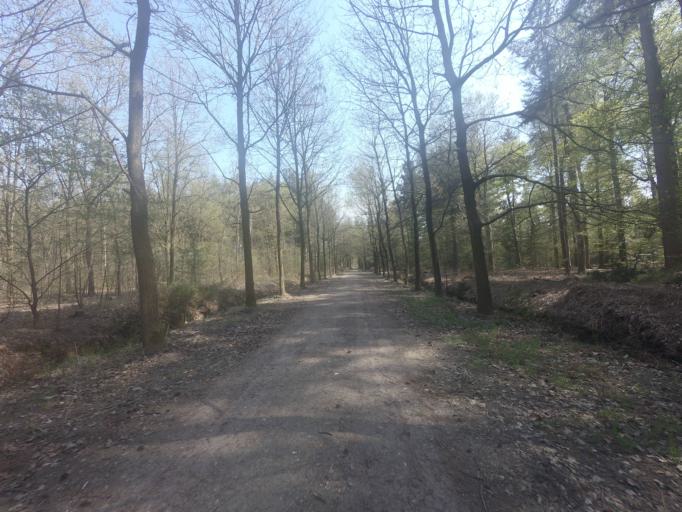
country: NL
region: Utrecht
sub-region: Gemeente Soest
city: Soest
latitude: 52.1795
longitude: 5.2502
